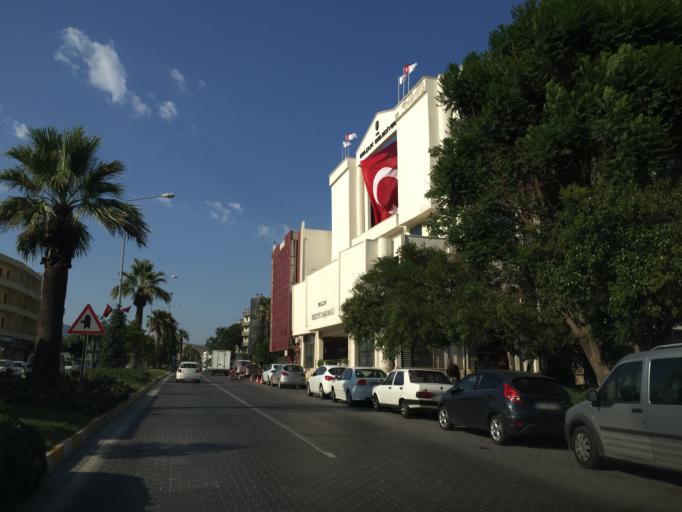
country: TR
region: Izmir
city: Selcuk
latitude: 37.9497
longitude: 27.3694
